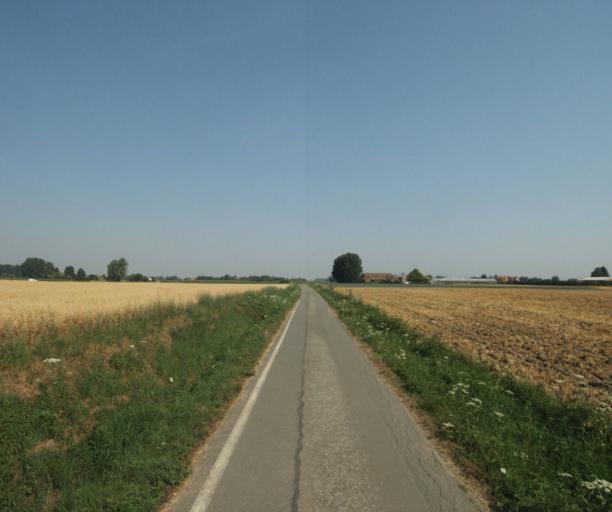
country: FR
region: Nord-Pas-de-Calais
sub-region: Departement du Nord
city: Verlinghem
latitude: 50.6970
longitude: 2.9865
